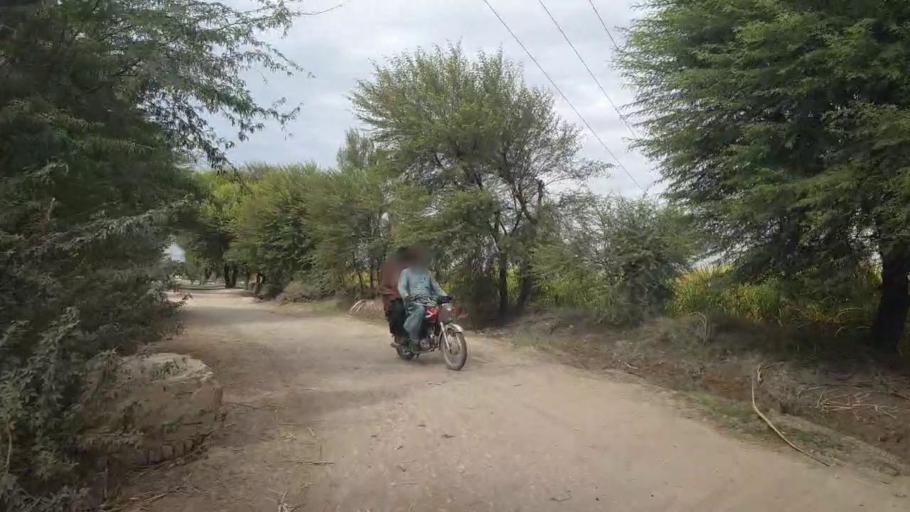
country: PK
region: Sindh
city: Jhol
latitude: 26.0054
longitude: 68.8746
